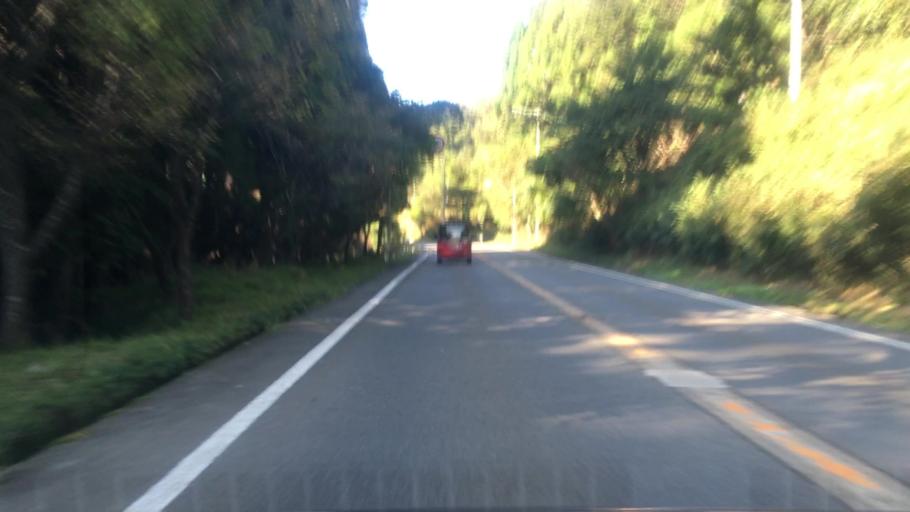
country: JP
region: Hyogo
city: Toyooka
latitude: 35.5651
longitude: 134.8526
